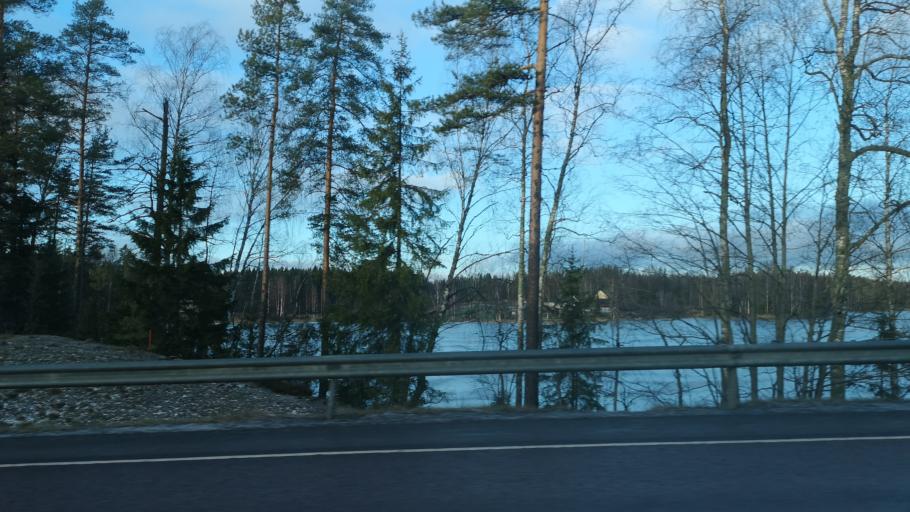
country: FI
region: Paijanne Tavastia
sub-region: Lahti
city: Heinola
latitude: 61.3368
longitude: 26.1789
